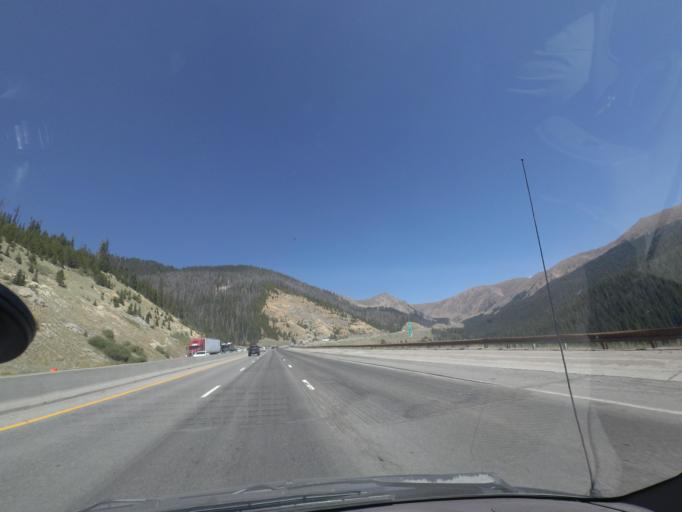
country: US
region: Colorado
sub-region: Summit County
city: Keystone
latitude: 39.6706
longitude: -105.9739
